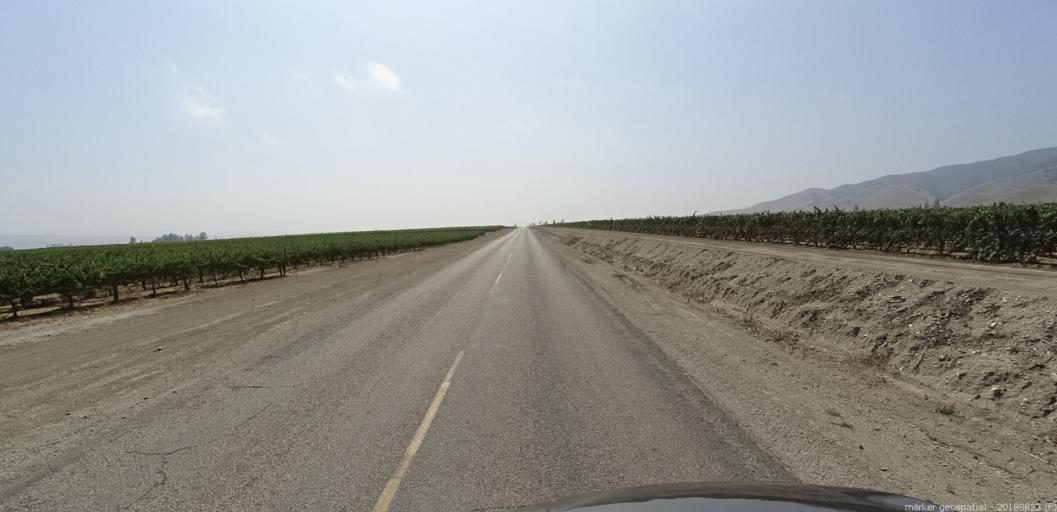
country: US
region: California
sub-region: Monterey County
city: Greenfield
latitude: 36.2691
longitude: -121.2178
